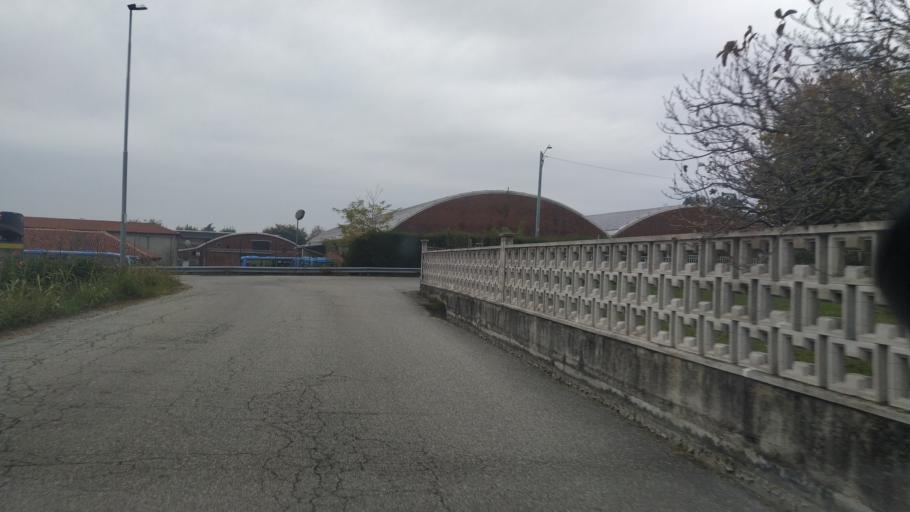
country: IT
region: Piedmont
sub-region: Provincia di Vercelli
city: Alice Castello
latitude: 45.3638
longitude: 8.0779
